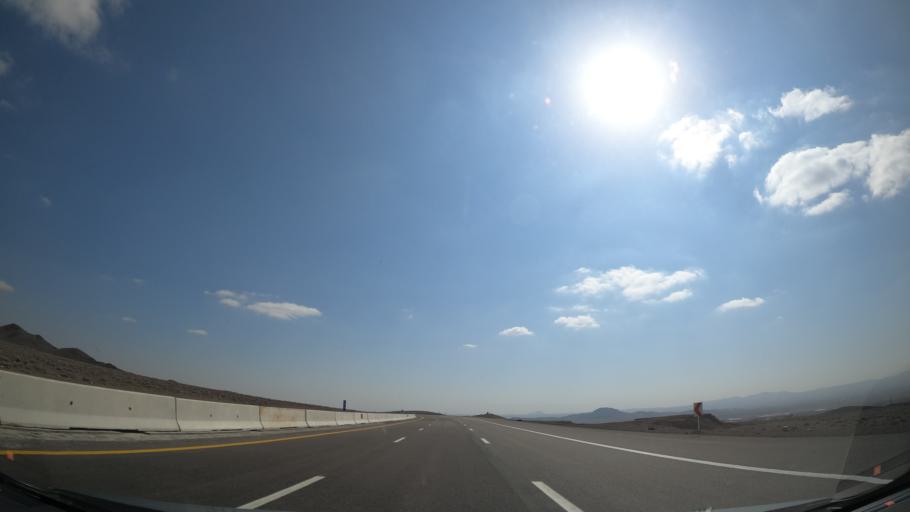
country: IR
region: Alborz
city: Eshtehard
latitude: 35.6712
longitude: 50.6454
